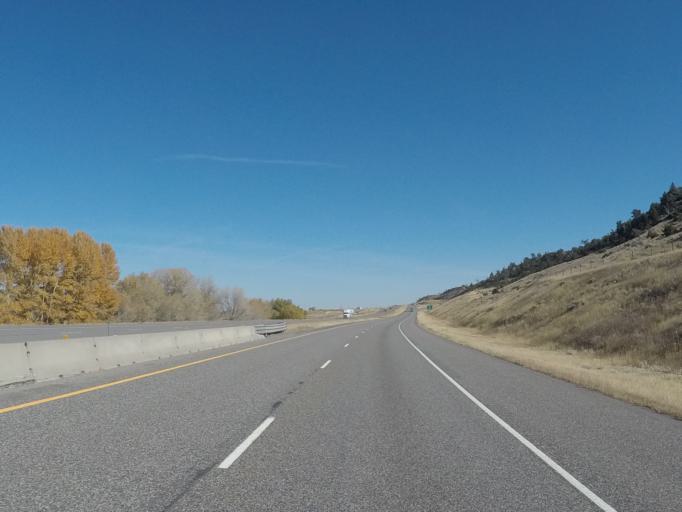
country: US
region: Montana
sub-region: Sweet Grass County
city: Big Timber
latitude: 45.7345
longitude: -110.2274
